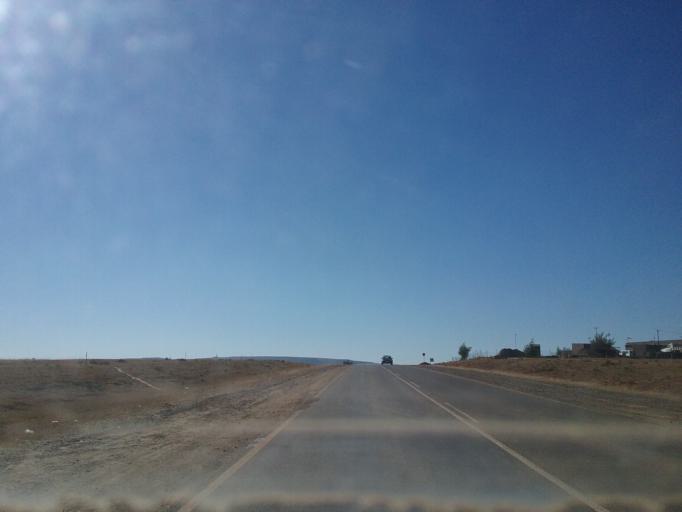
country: LS
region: Maseru
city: Maseru
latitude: -29.4299
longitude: 27.5660
